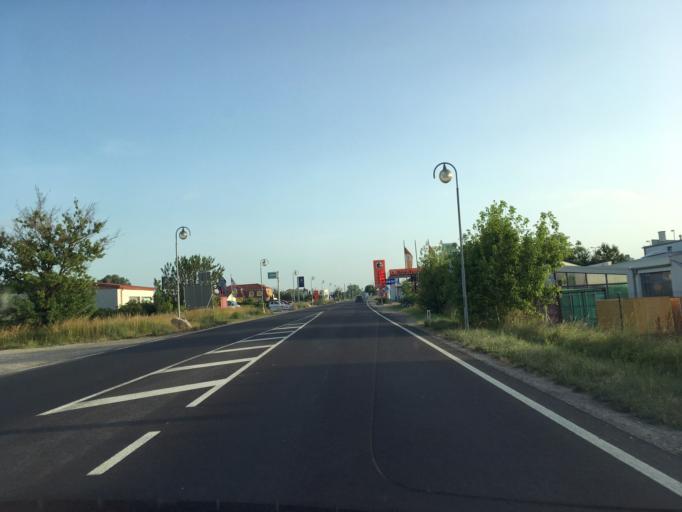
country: AT
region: Lower Austria
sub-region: Politischer Bezirk Baden
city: Traiskirchen
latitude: 47.9826
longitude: 16.2891
